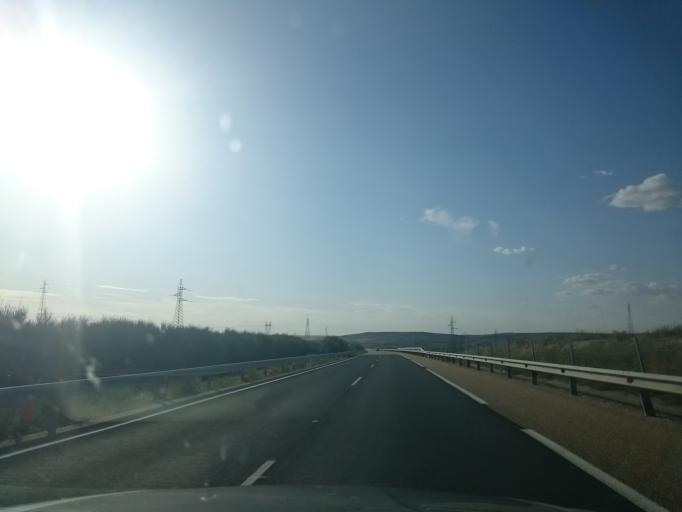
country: ES
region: Castille and Leon
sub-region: Provincia de Burgos
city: Villalbilla de Burgos
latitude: 42.3290
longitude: -3.7736
